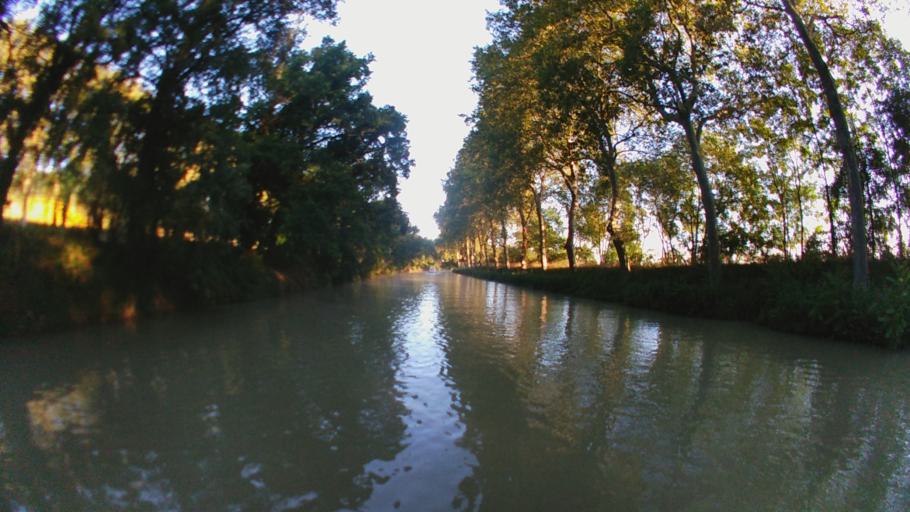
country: FR
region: Midi-Pyrenees
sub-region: Departement de la Haute-Garonne
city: Gardouch
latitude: 43.4030
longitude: 1.6702
